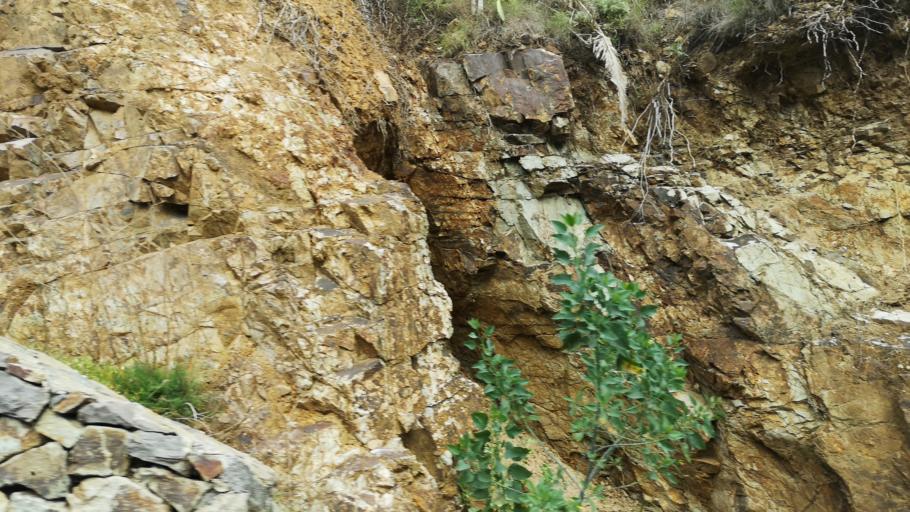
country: ES
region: Canary Islands
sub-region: Provincia de Santa Cruz de Tenerife
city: Vallehermosa
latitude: 28.1723
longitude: -17.2748
